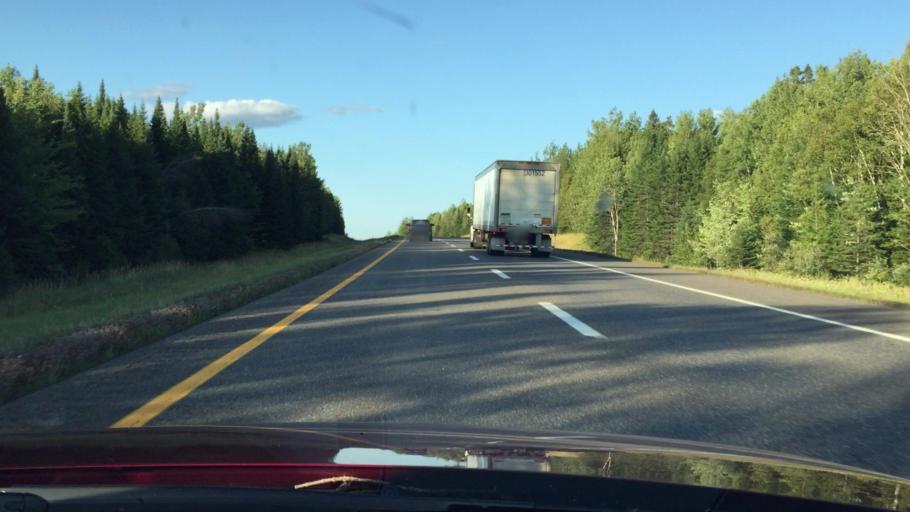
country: US
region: Maine
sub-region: Penobscot County
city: Patten
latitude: 46.0289
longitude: -68.2791
